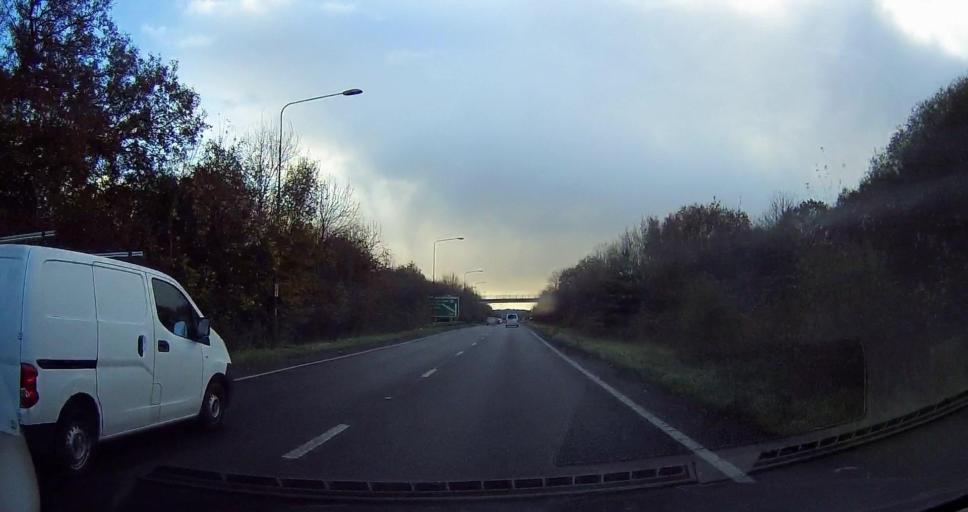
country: GB
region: England
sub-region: West Sussex
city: Hurstpierpoint
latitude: 50.9630
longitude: -0.1936
